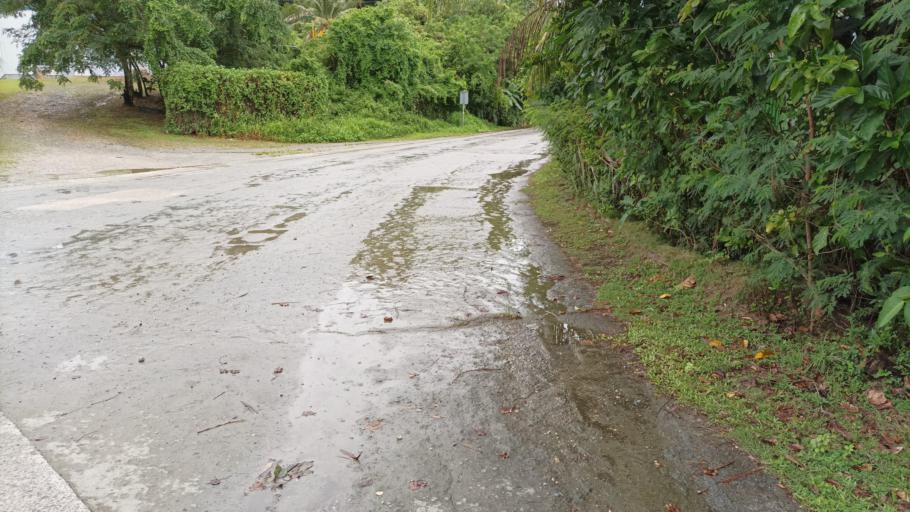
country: FM
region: Yap
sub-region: Weloy Municipality
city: Colonia
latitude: 9.5146
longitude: 138.1210
